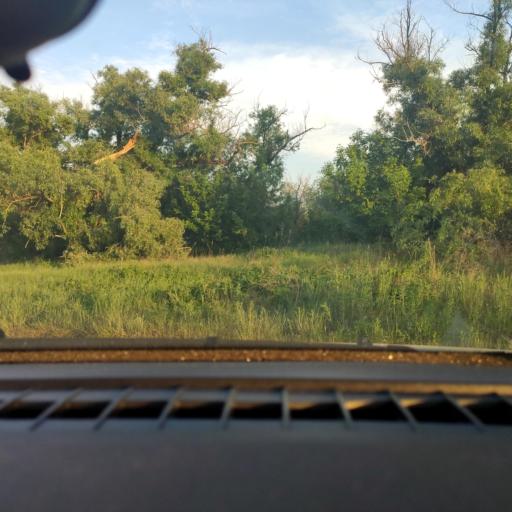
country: RU
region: Voronezj
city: Shilovo
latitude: 51.5371
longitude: 39.1301
